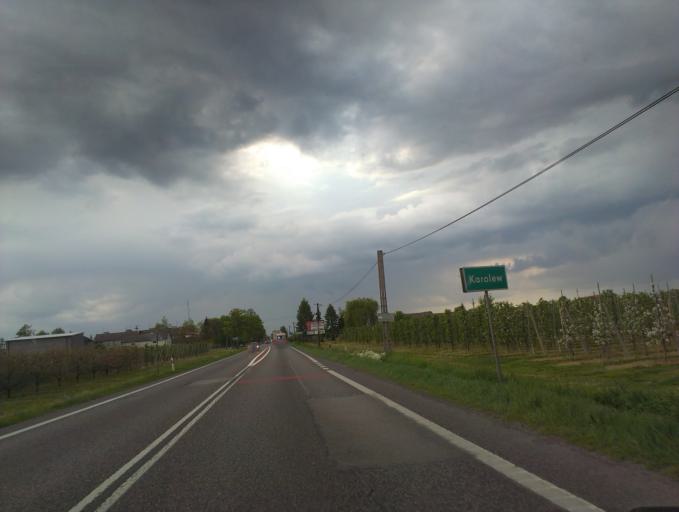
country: PL
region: Masovian Voivodeship
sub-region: Powiat grojecki
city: Pniewy
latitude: 51.9142
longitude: 20.6929
